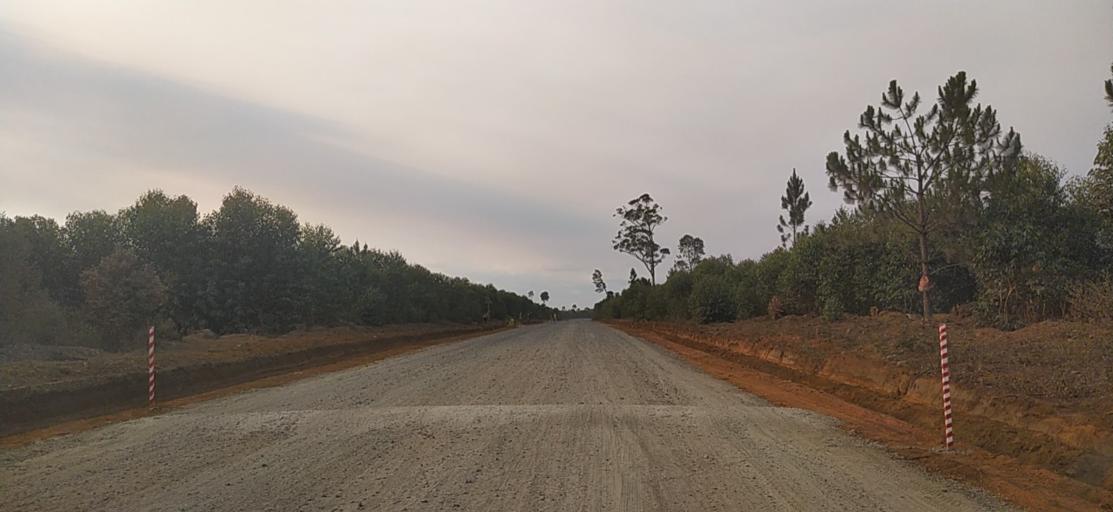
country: MG
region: Alaotra Mangoro
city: Moramanga
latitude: -18.5391
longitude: 48.2589
